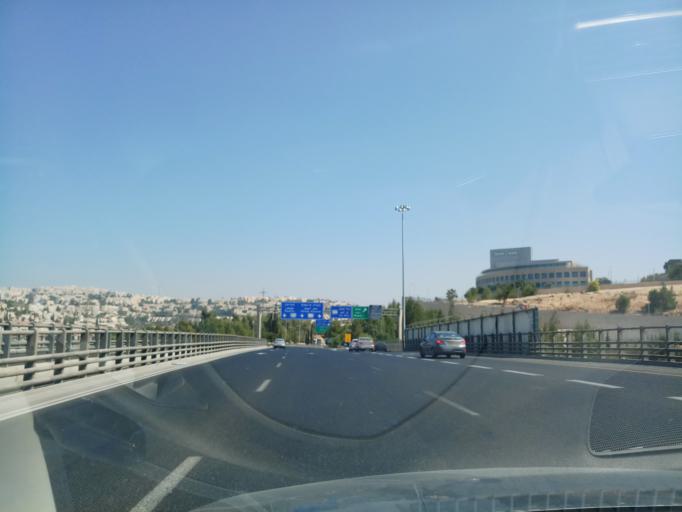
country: IL
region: Jerusalem
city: West Jerusalem
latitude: 31.8016
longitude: 35.2052
